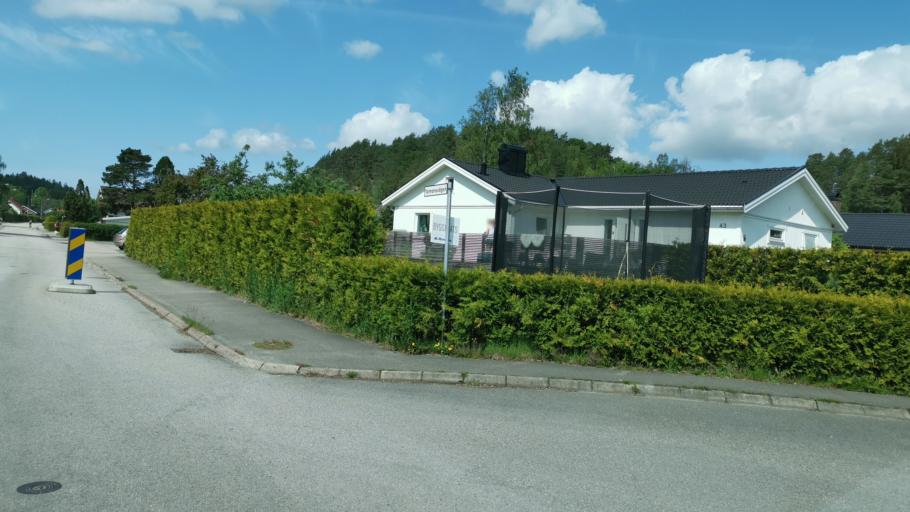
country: SE
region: Vaestra Goetaland
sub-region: Uddevalla Kommun
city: Uddevalla
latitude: 58.3536
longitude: 11.8491
